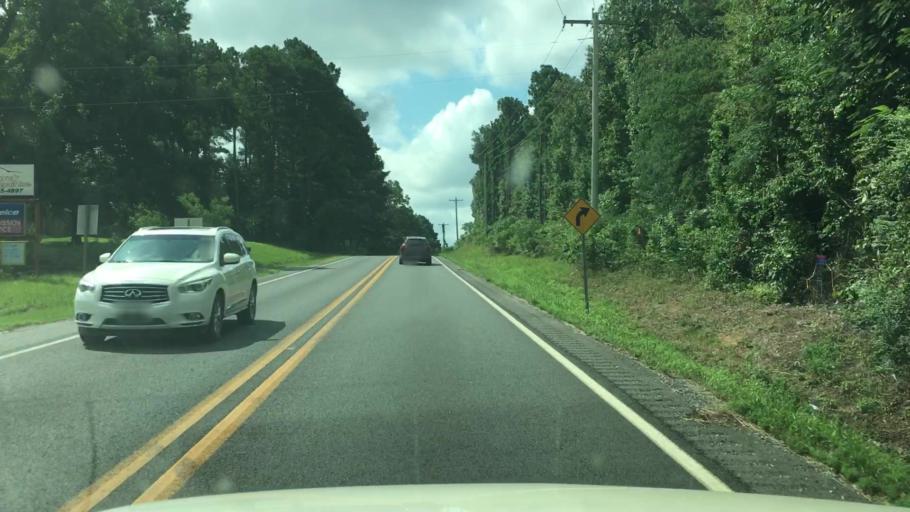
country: US
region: Arkansas
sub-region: Garland County
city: Lake Hamilton
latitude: 34.3125
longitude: -93.1694
